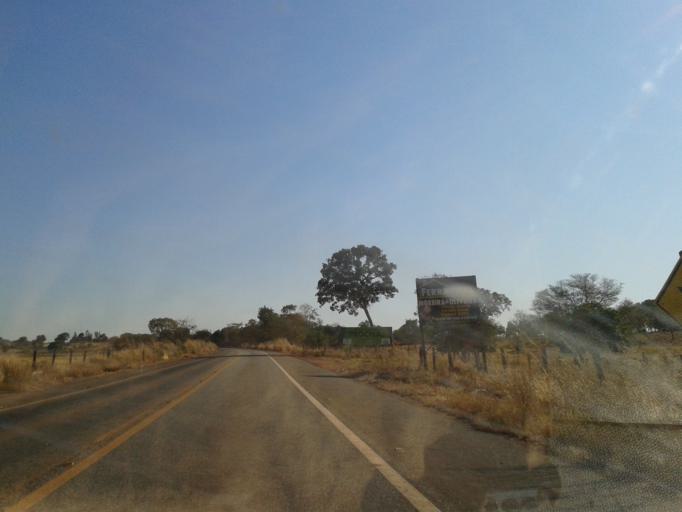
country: BR
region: Goias
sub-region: Mozarlandia
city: Mozarlandia
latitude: -14.7730
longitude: -50.5368
